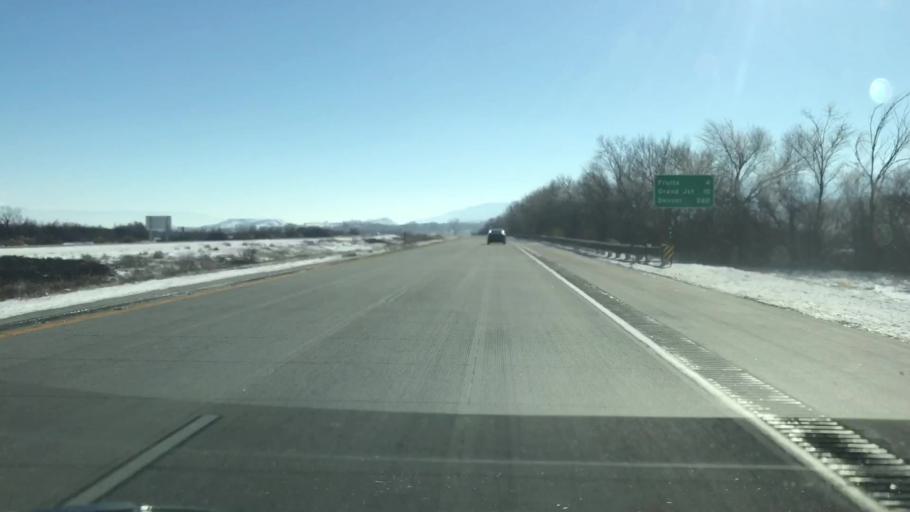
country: US
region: Colorado
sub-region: Mesa County
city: Loma
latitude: 39.1732
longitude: -108.7980
